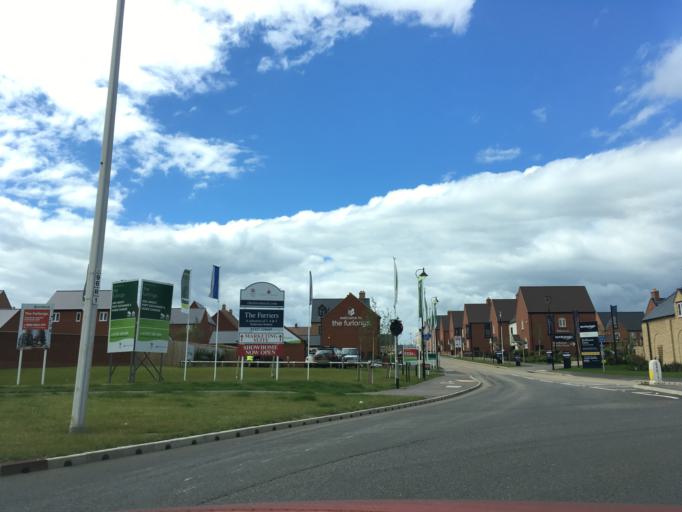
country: GB
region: England
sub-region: Northamptonshire
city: Towcester
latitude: 52.1222
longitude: -0.9731
